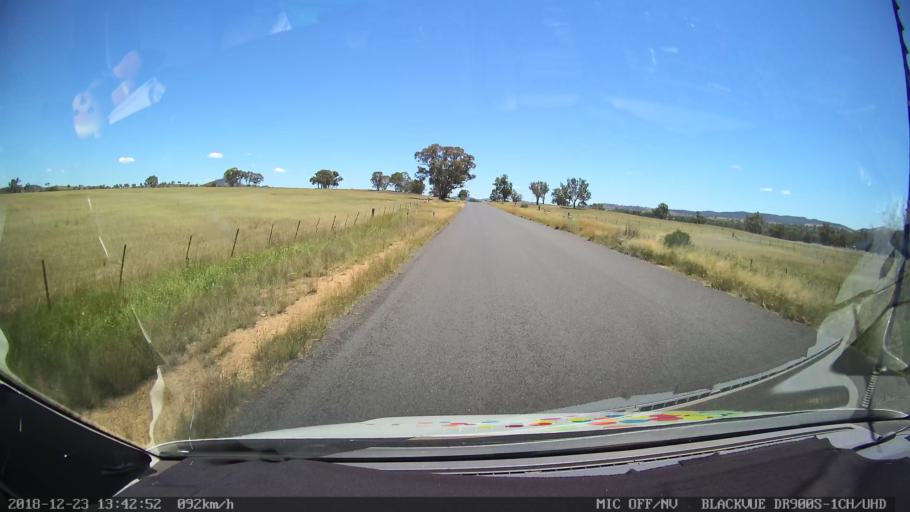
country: AU
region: New South Wales
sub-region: Tamworth Municipality
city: Manilla
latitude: -30.4814
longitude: 151.1577
